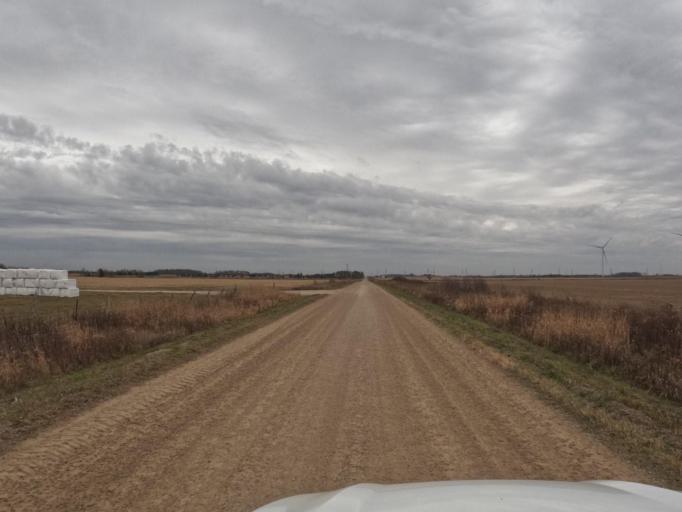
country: CA
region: Ontario
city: Shelburne
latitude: 44.0175
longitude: -80.3911
